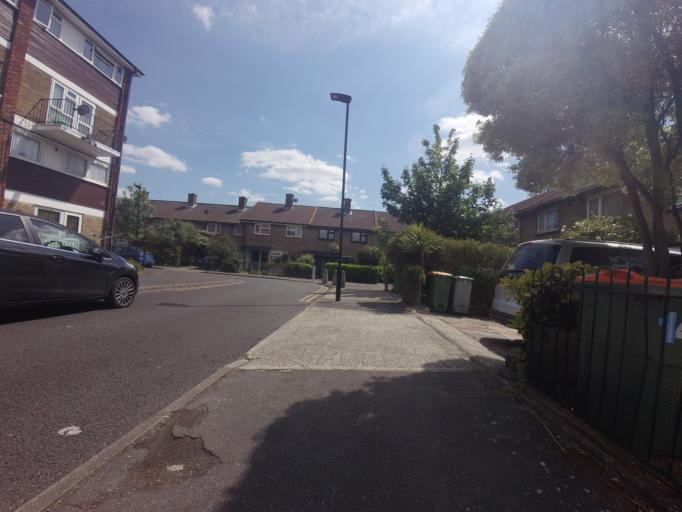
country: GB
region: England
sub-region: Greater London
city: East Ham
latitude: 51.5536
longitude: 0.0192
